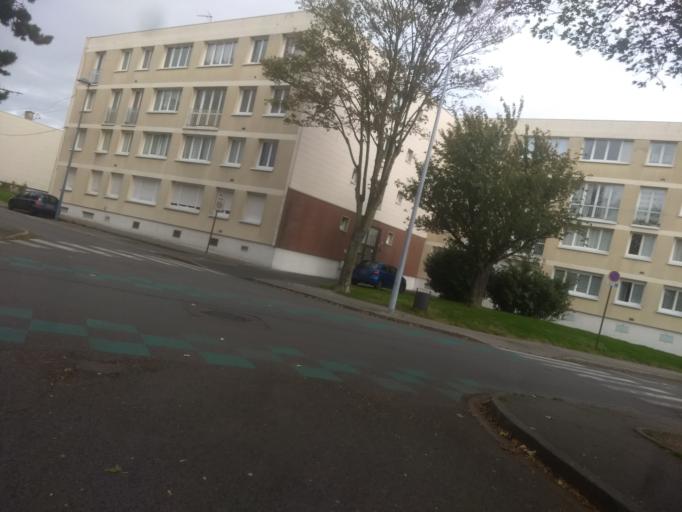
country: FR
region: Nord-Pas-de-Calais
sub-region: Departement du Pas-de-Calais
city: Achicourt
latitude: 50.2912
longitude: 2.7500
